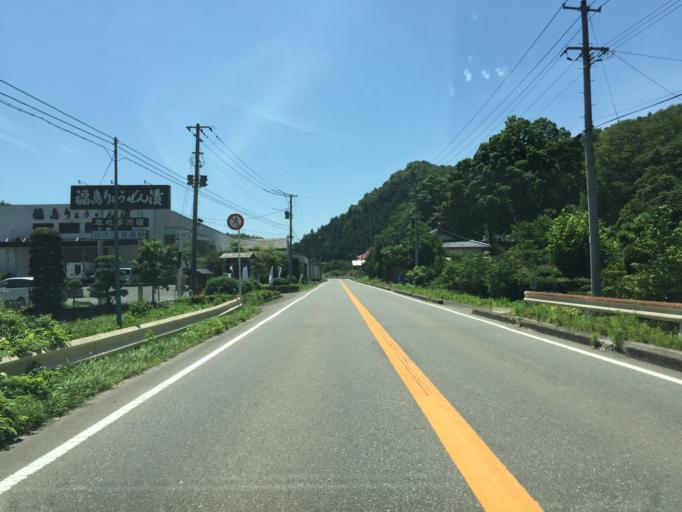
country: JP
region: Fukushima
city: Hobaramachi
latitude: 37.7641
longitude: 140.5660
